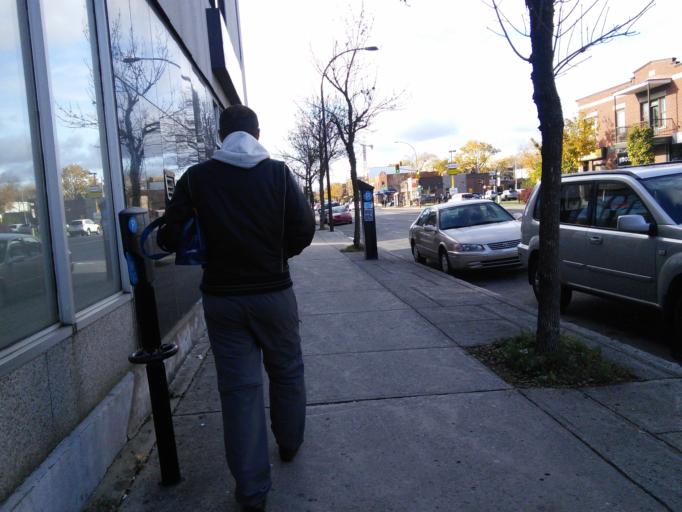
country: CA
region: Quebec
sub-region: Montreal
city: Montreal
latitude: 45.5381
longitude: -73.6145
